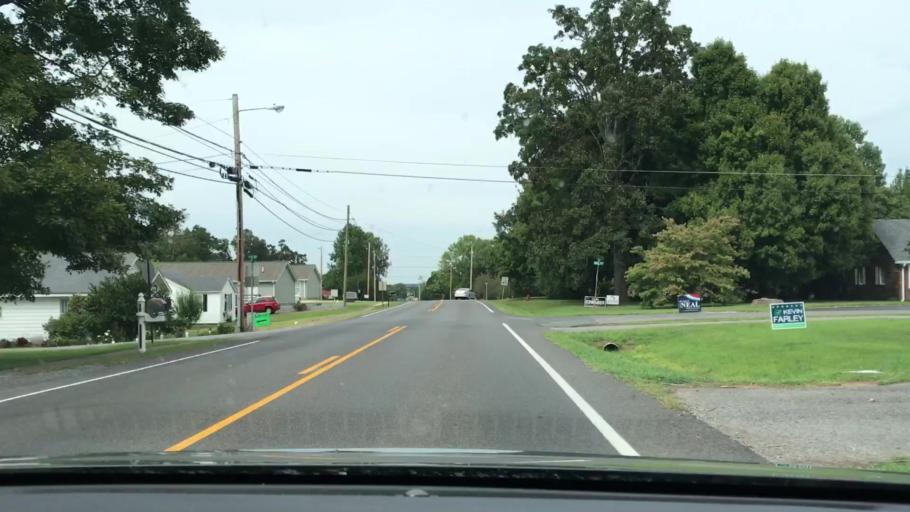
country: US
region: Kentucky
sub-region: Marshall County
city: Benton
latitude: 36.8459
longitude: -88.3498
